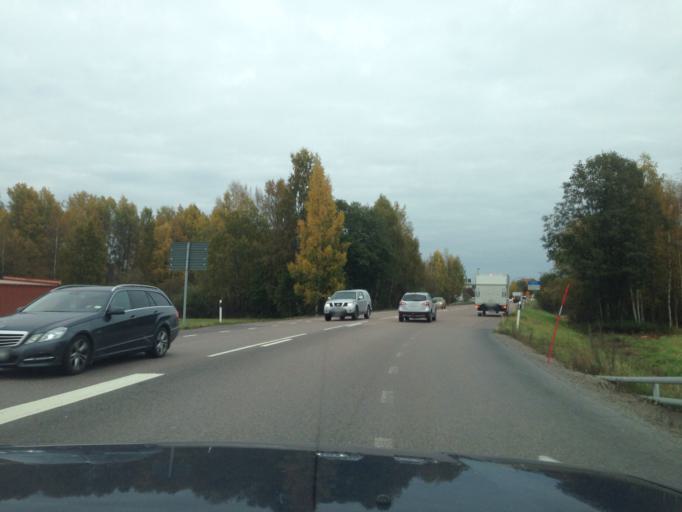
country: SE
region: Dalarna
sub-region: Borlange Kommun
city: Borlaenge
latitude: 60.4795
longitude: 15.4121
